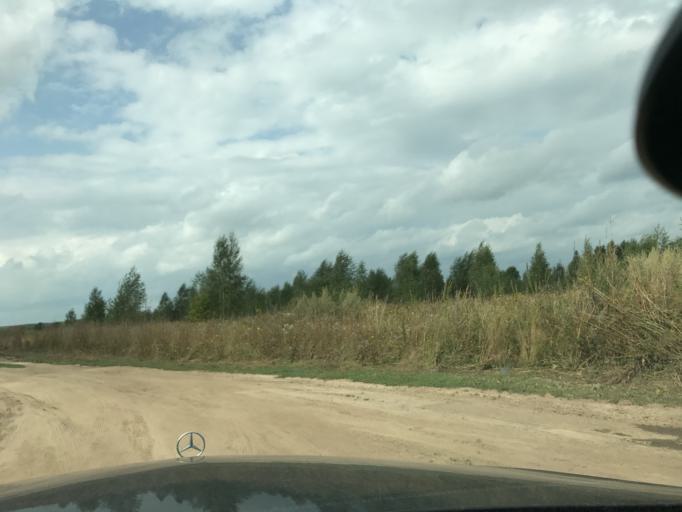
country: RU
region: Nizjnij Novgorod
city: Vacha
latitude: 55.9826
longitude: 42.7906
